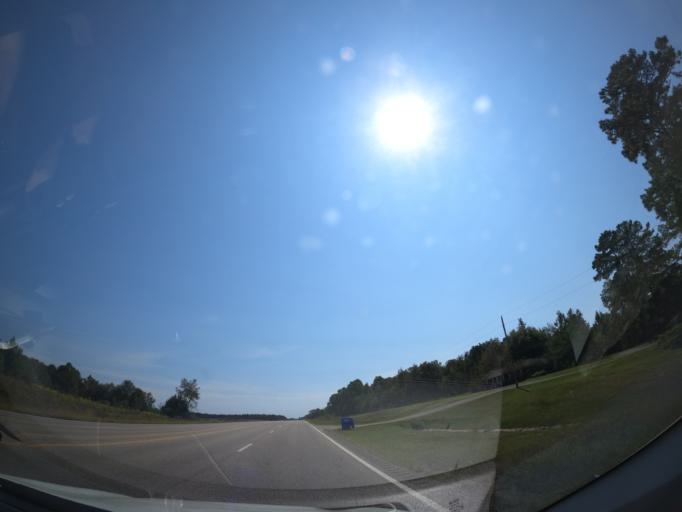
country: US
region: Alabama
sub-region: Covington County
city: Andalusia
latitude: 31.3875
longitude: -86.5708
